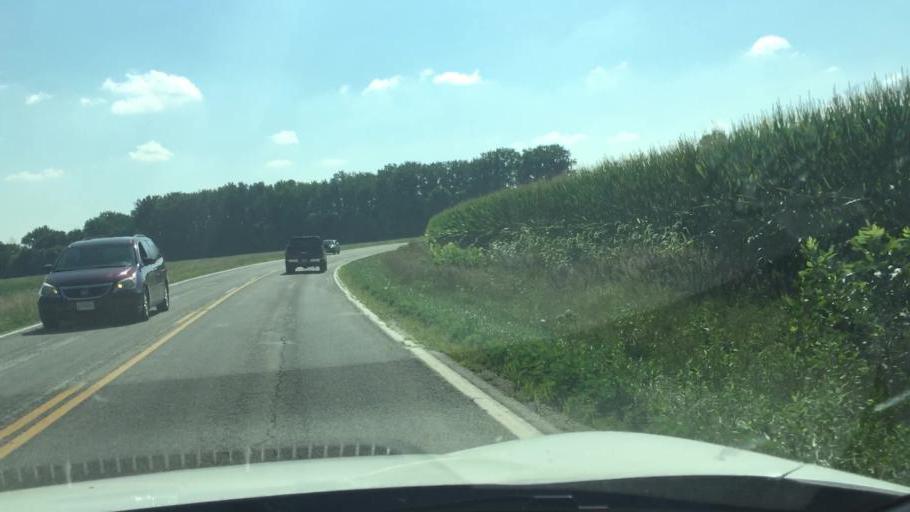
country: US
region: Ohio
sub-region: Champaign County
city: North Lewisburg
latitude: 40.2284
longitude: -83.5174
